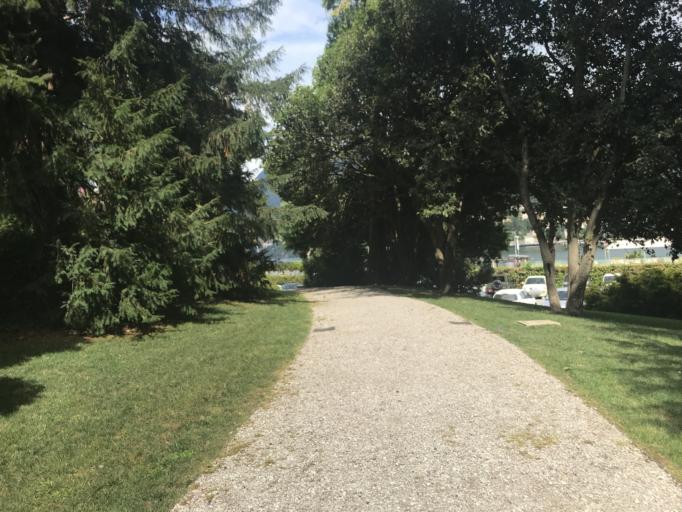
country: IT
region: Lombardy
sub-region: Provincia di Como
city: San Fermo della Battaglia
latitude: 45.8199
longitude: 9.0657
